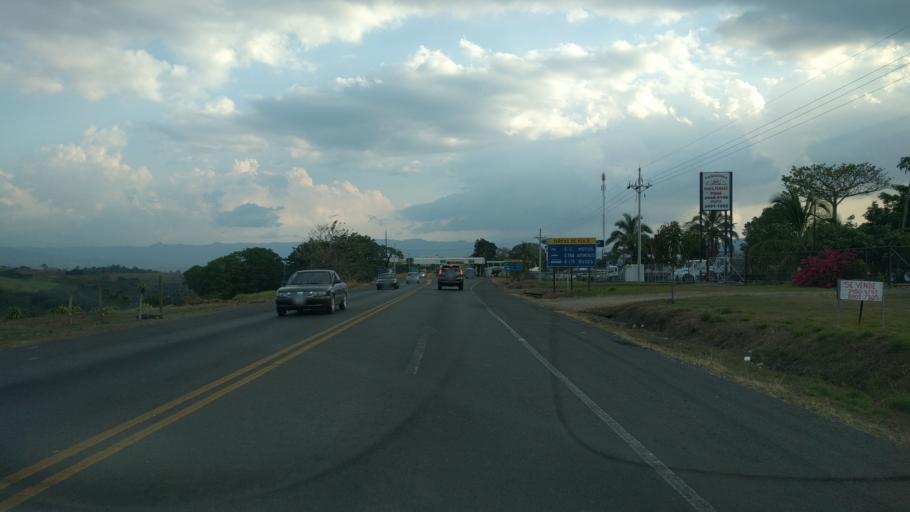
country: CR
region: Alajuela
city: Naranjo
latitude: 10.0574
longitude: -84.3610
